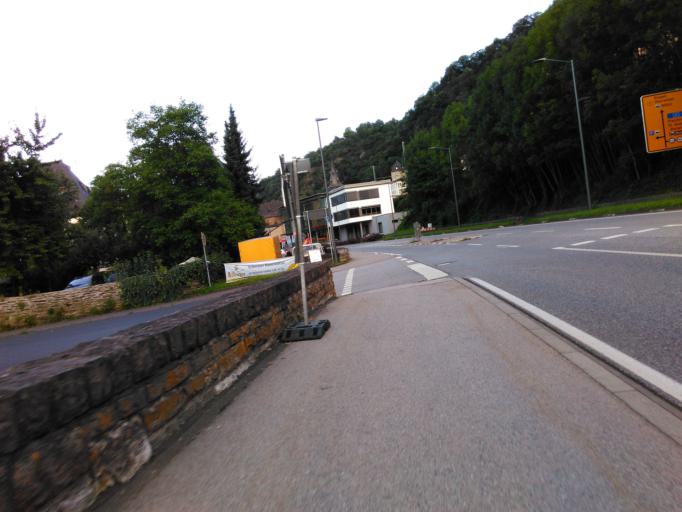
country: DE
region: Rheinland-Pfalz
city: Sankt Goar
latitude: 50.1533
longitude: 7.7083
